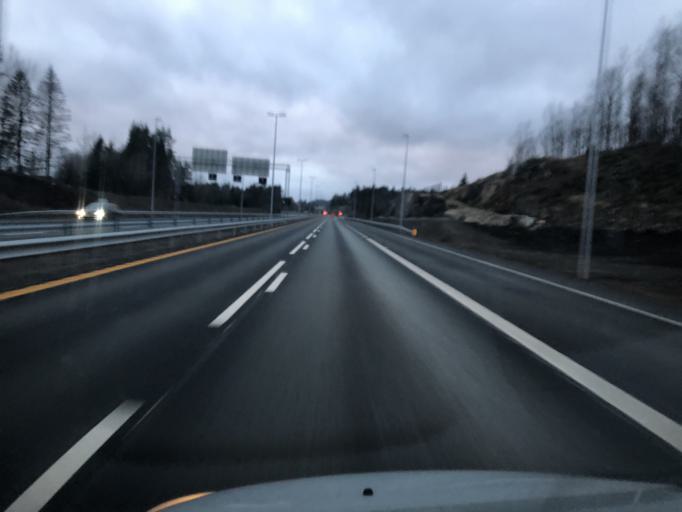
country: NO
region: Aust-Agder
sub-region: Arendal
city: Arendal
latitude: 58.4999
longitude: 8.7892
